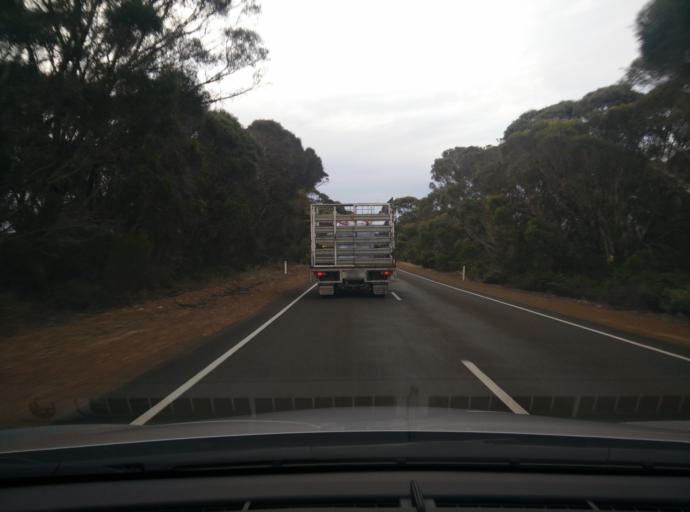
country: AU
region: South Australia
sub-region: Kangaroo Island
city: Kingscote
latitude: -35.7507
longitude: 137.5948
